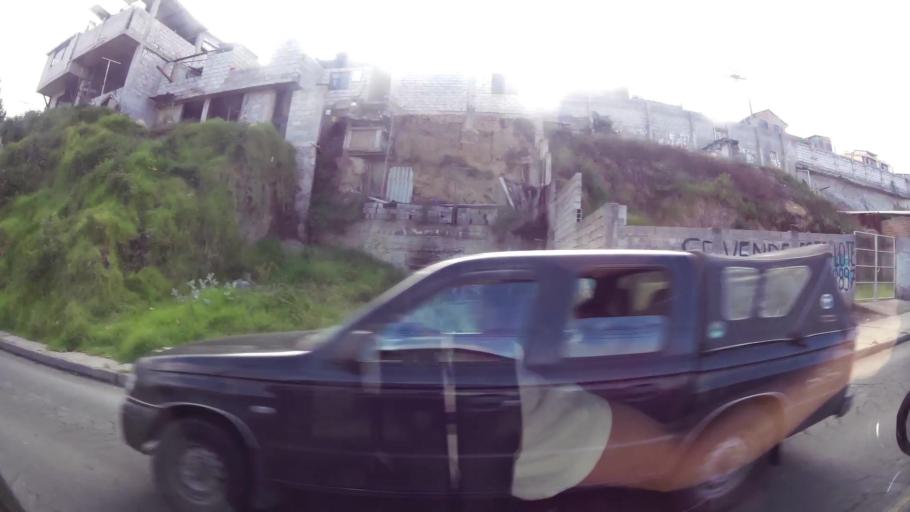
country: EC
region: Pichincha
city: Quito
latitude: -0.2533
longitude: -78.4958
